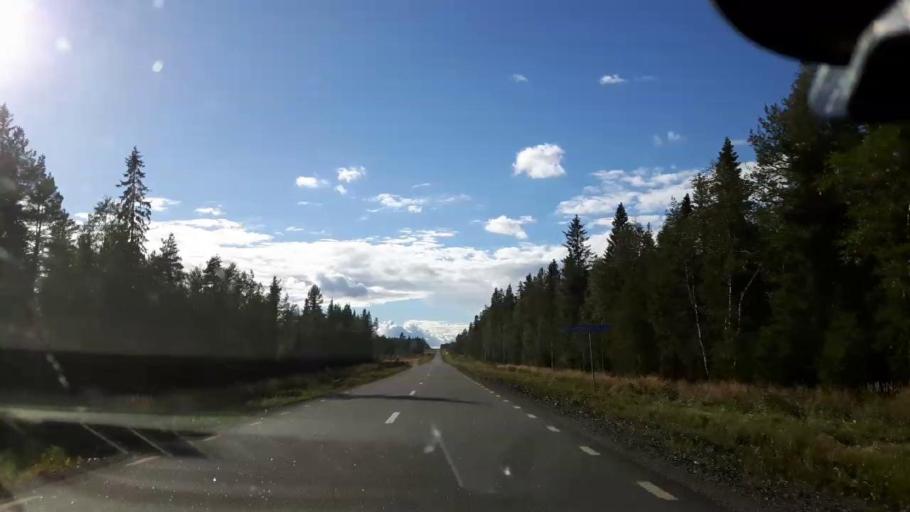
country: SE
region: Jaemtland
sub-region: Stroemsunds Kommun
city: Stroemsund
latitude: 63.5408
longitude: 15.9672
